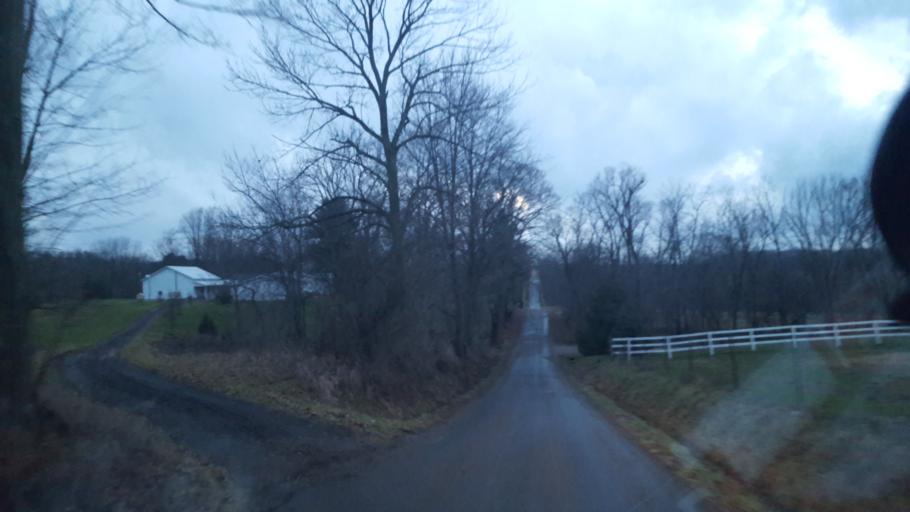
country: US
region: Ohio
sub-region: Richland County
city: Lexington
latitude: 40.6122
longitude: -82.6079
